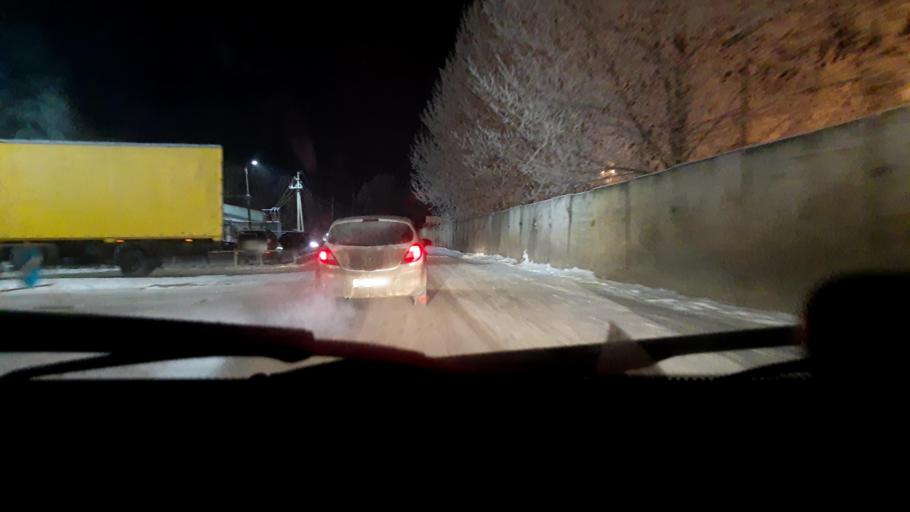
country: RU
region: Bashkortostan
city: Mikhaylovka
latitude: 54.7938
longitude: 55.8530
